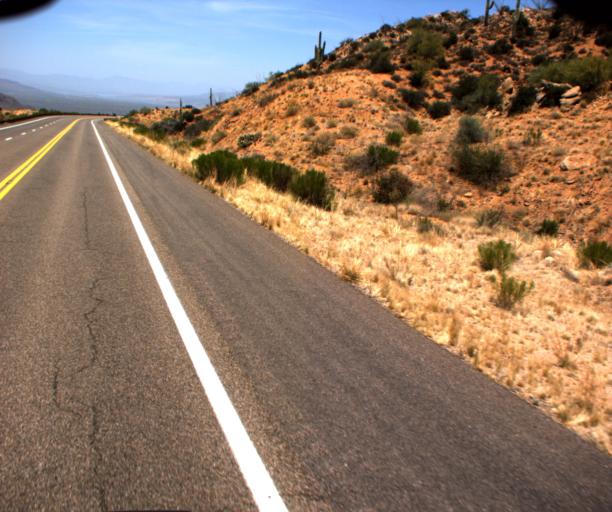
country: US
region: Arizona
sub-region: Gila County
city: Miami
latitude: 33.5475
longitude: -110.9441
